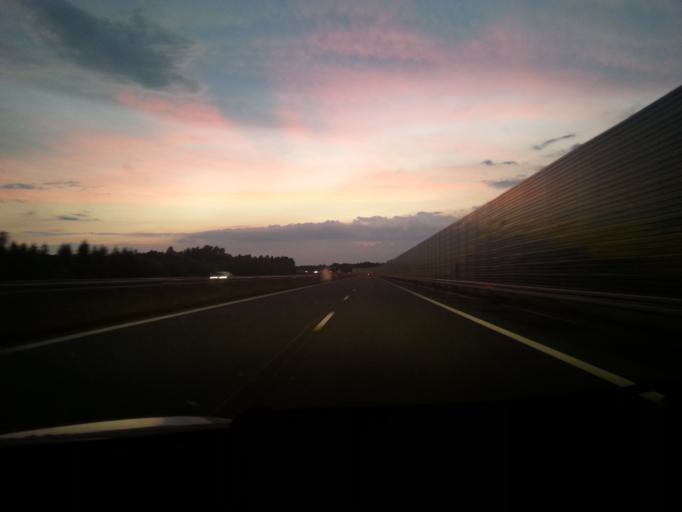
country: PL
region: Lodz Voivodeship
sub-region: Powiat zdunskowolski
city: Zdunska Wola
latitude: 51.5887
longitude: 18.8944
